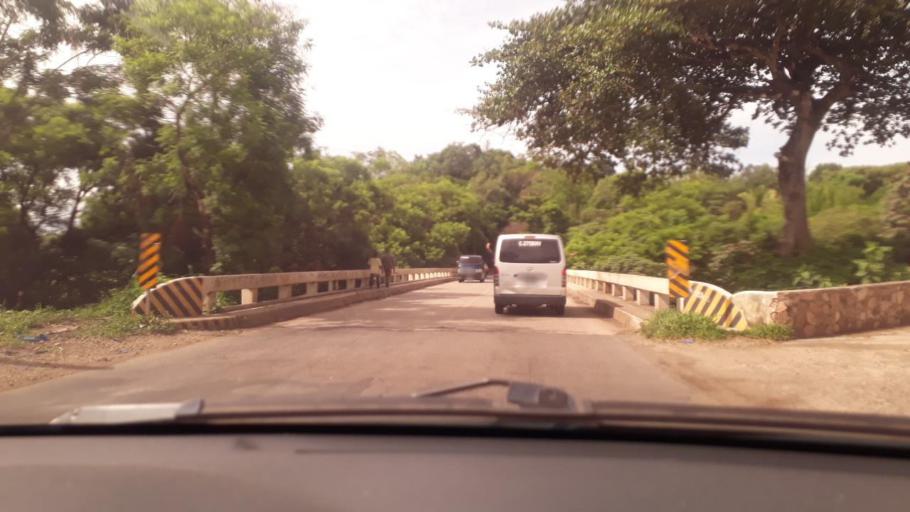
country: GT
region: Jutiapa
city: Quesada
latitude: 14.2731
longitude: -90.0042
